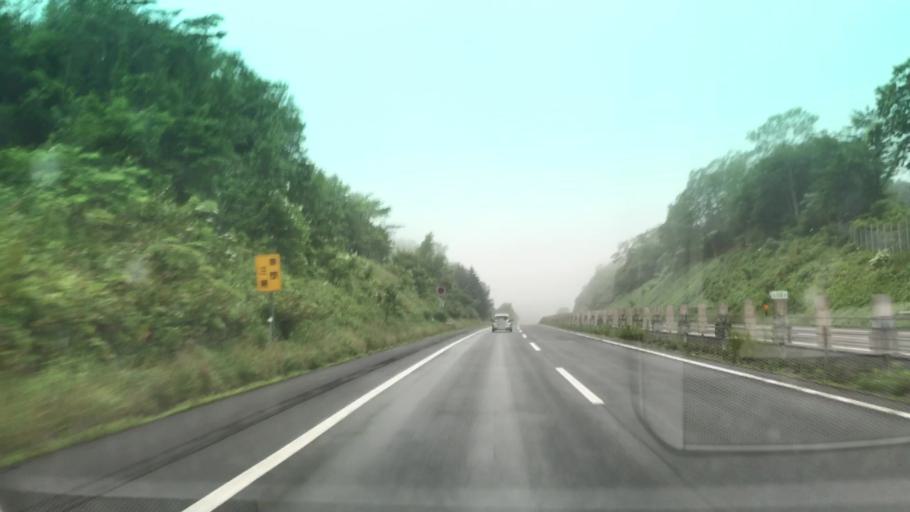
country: JP
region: Hokkaido
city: Tomakomai
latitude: 42.6521
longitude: 141.5586
